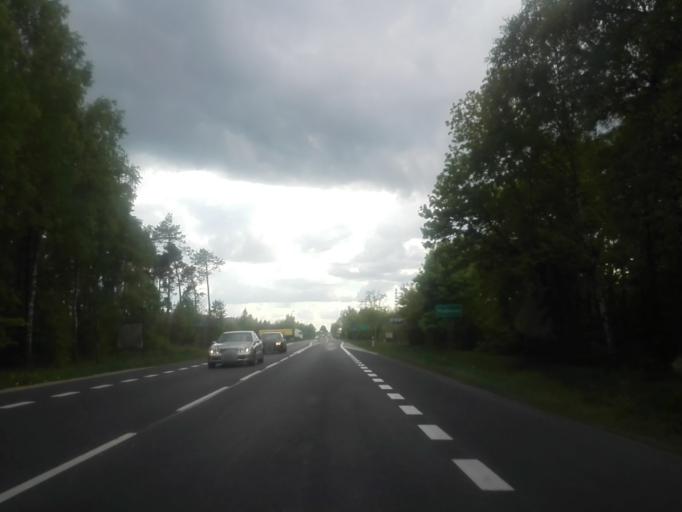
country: PL
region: Masovian Voivodeship
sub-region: Powiat ostrowski
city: Ostrow Mazowiecka
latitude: 52.8292
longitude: 21.9409
